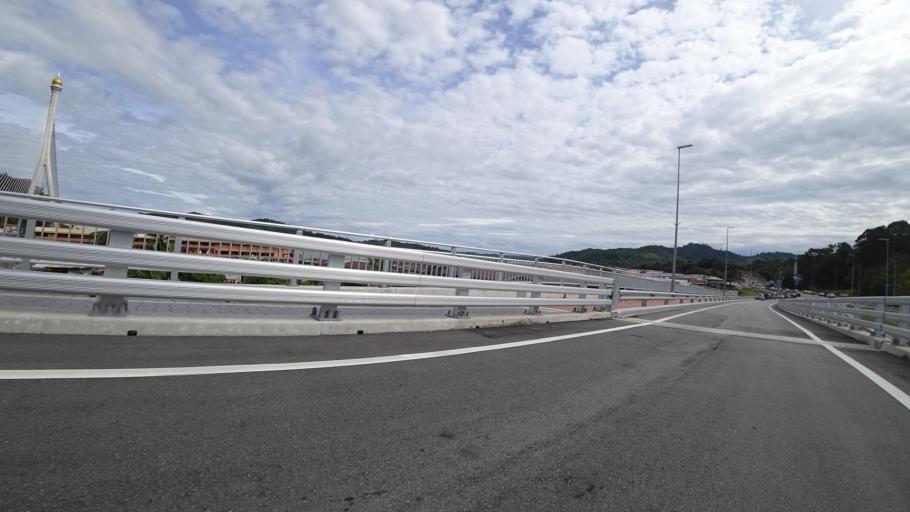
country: BN
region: Brunei and Muara
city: Bandar Seri Begawan
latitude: 4.8764
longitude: 114.9459
